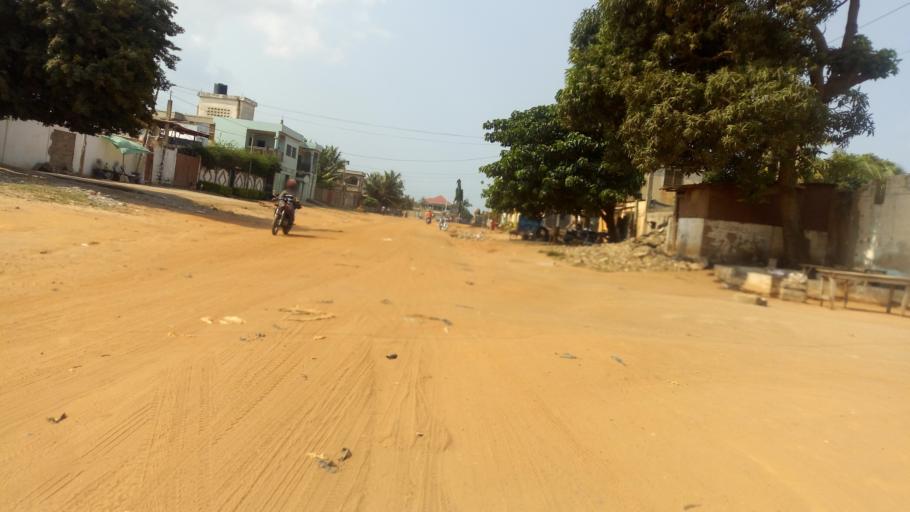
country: TG
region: Maritime
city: Lome
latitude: 6.1968
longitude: 1.1830
